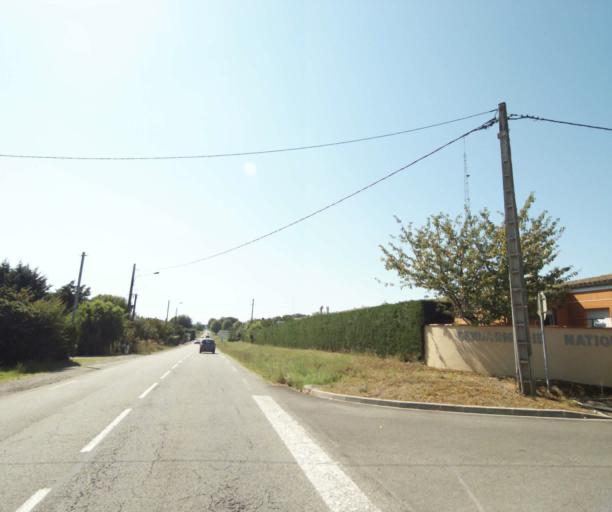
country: FR
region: Midi-Pyrenees
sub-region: Departement de l'Ariege
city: Lezat-sur-Leze
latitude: 43.2708
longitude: 1.3491
